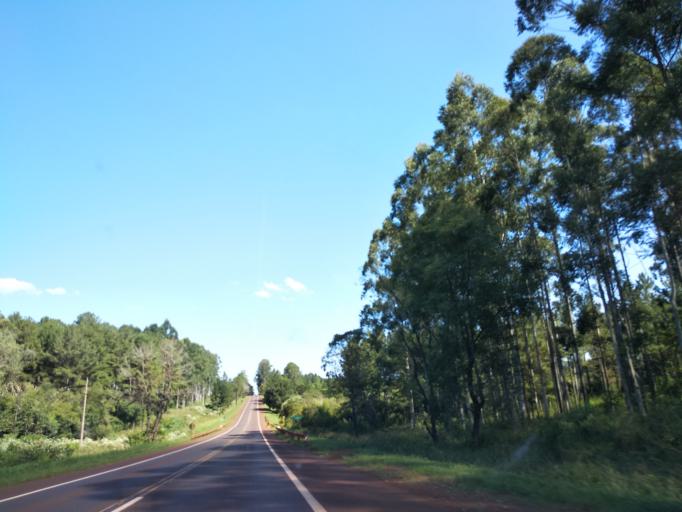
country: AR
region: Misiones
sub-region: Departamento de Montecarlo
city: Montecarlo
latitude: -26.5555
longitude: -54.7248
